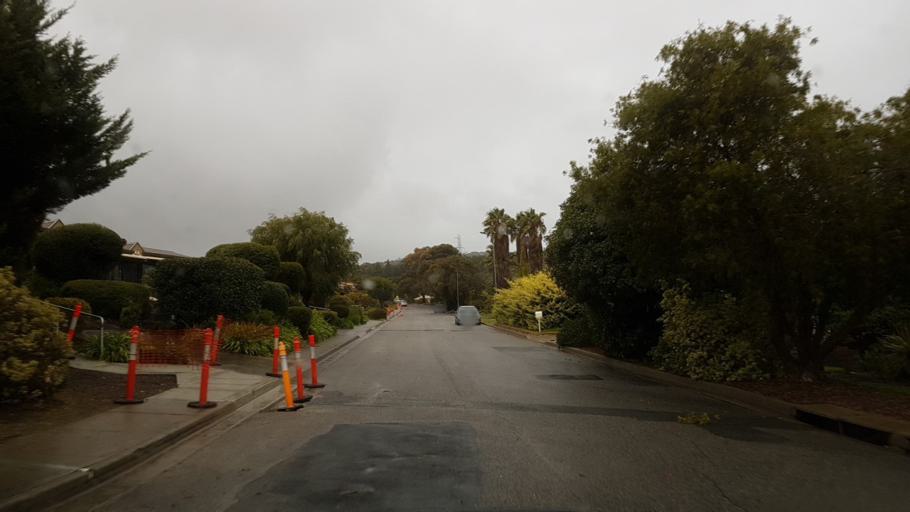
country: AU
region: South Australia
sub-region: Marion
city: Trott Park
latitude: -35.0929
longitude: 138.5887
